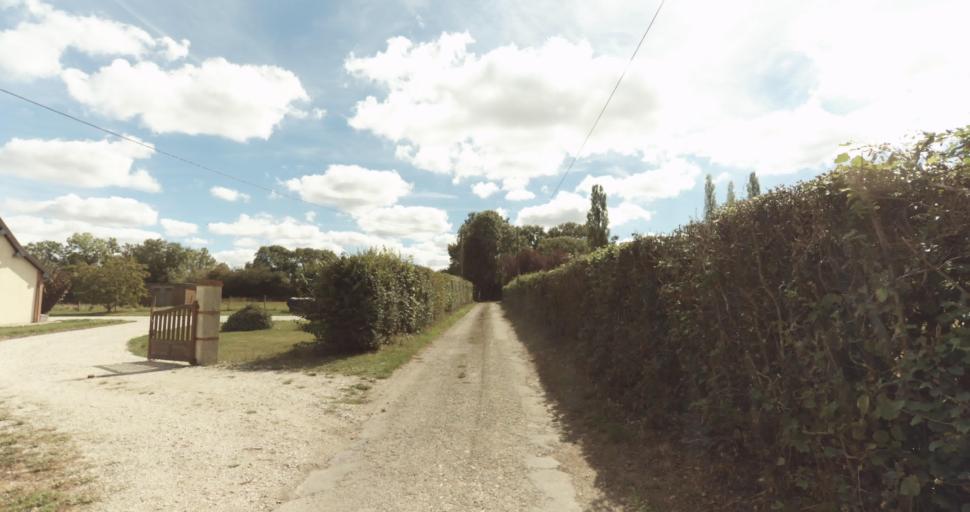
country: FR
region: Lower Normandy
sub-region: Departement de l'Orne
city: Gace
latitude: 48.8950
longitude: 0.3592
